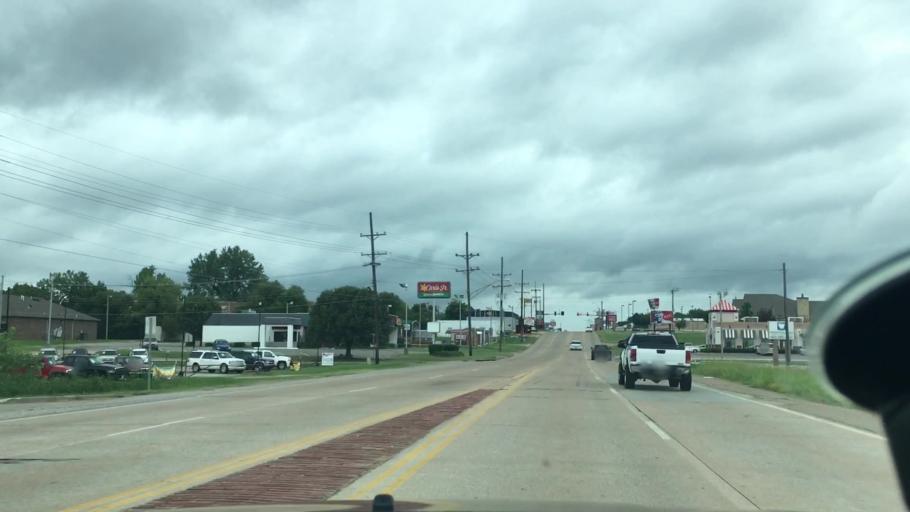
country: US
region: Oklahoma
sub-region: Seminole County
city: Seminole
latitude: 35.2351
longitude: -96.6711
